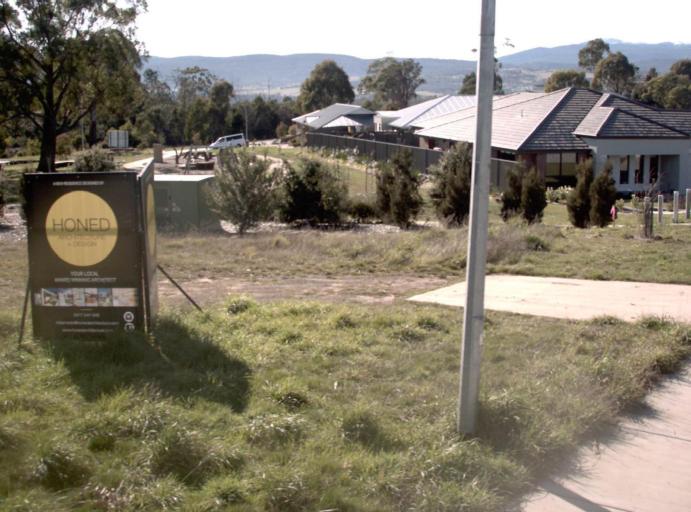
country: AU
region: Tasmania
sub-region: Launceston
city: Summerhill
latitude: -41.4764
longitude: 147.1510
